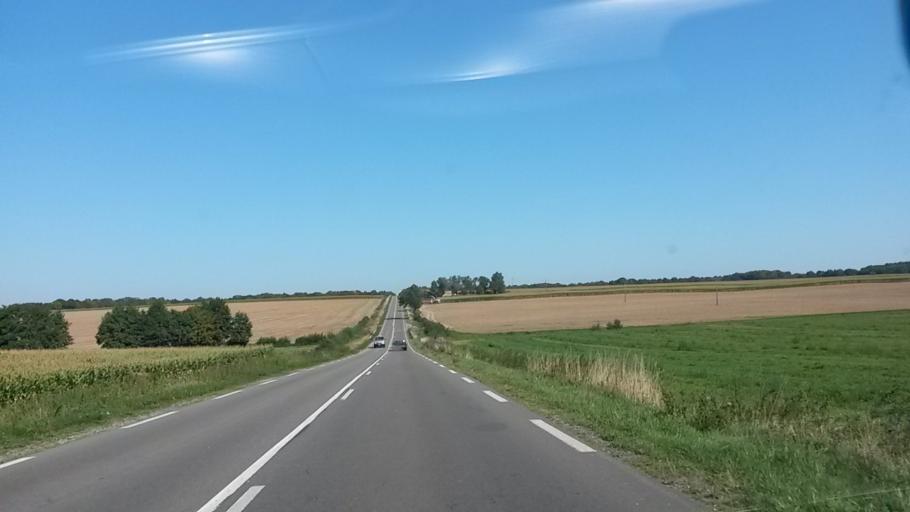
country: FR
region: Nord-Pas-de-Calais
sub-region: Departement du Nord
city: Avesnelles
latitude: 50.1811
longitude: 3.9524
